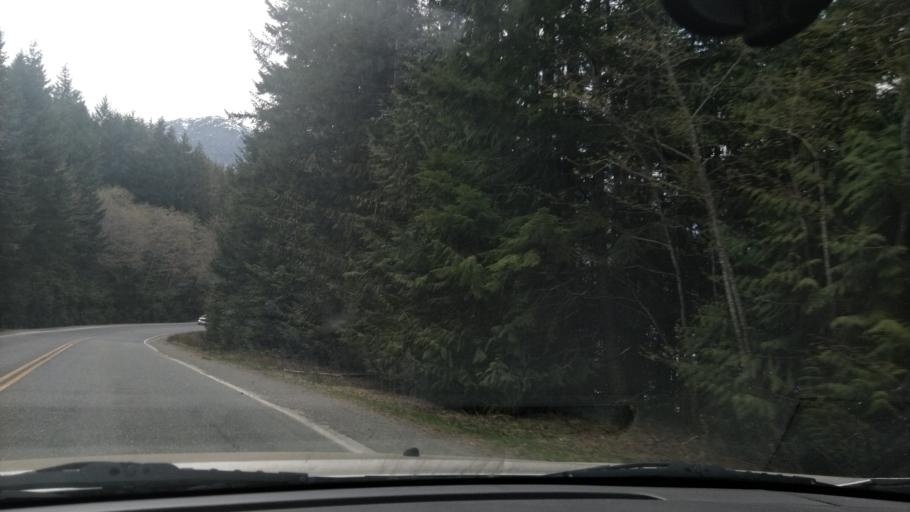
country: CA
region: British Columbia
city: Campbell River
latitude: 49.8819
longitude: -125.6877
